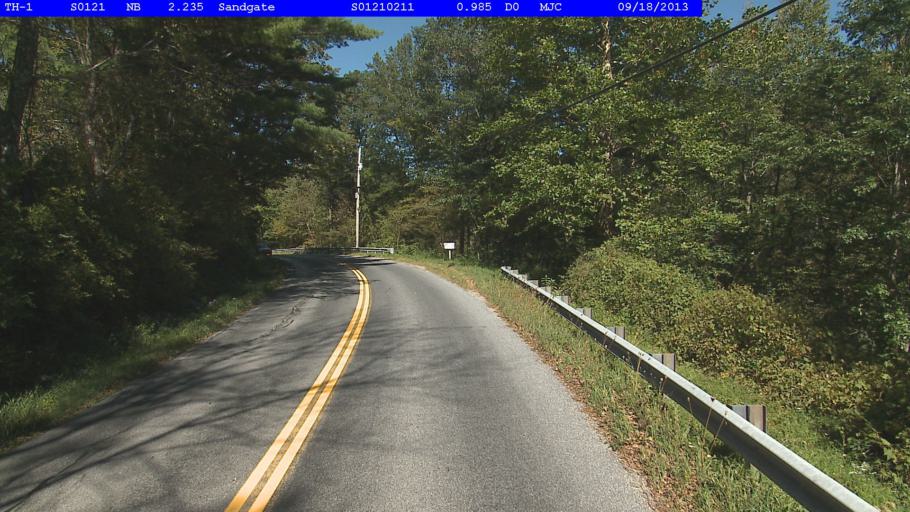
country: US
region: Vermont
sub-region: Bennington County
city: Arlington
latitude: 43.1343
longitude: -73.2042
